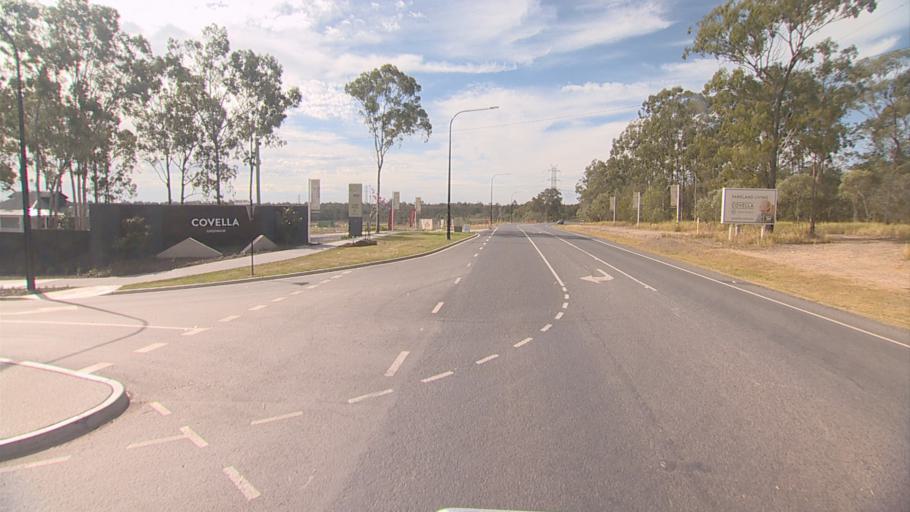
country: AU
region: Queensland
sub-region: Logan
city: North Maclean
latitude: -27.7368
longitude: 152.9745
